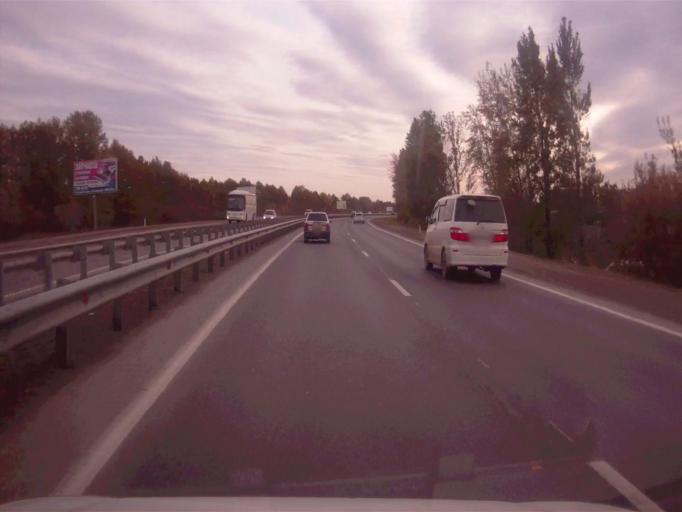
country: RU
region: Chelyabinsk
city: Novosineglazovskiy
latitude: 55.0287
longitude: 61.4484
